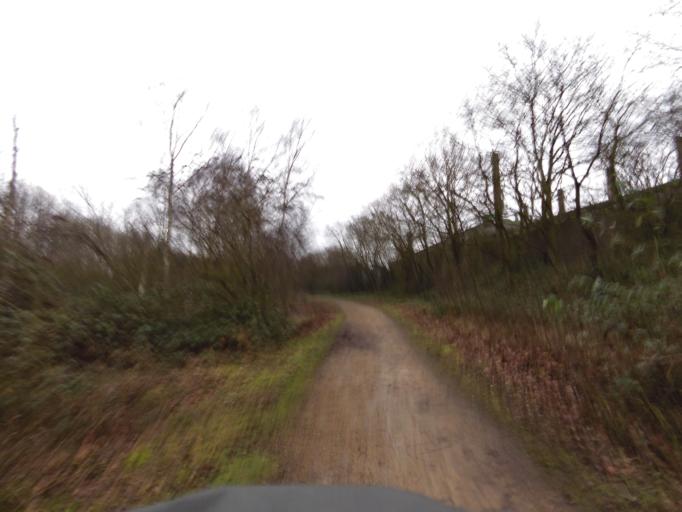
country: GB
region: England
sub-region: Norfolk
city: Costessey
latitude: 52.7166
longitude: 1.1337
